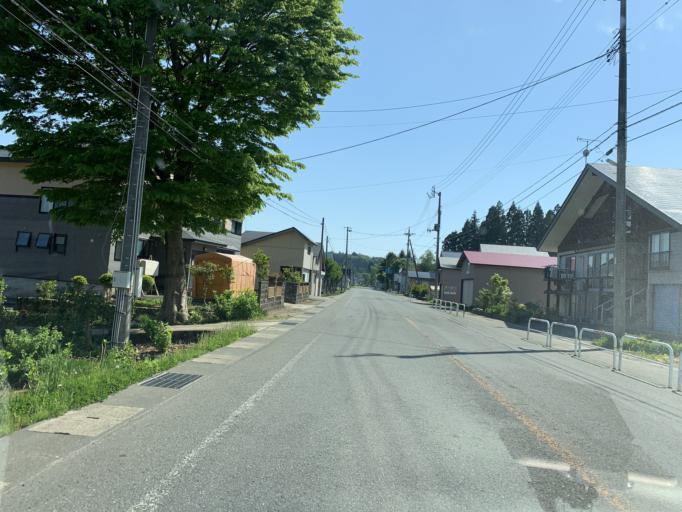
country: JP
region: Akita
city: Yokotemachi
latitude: 39.4256
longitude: 140.7475
